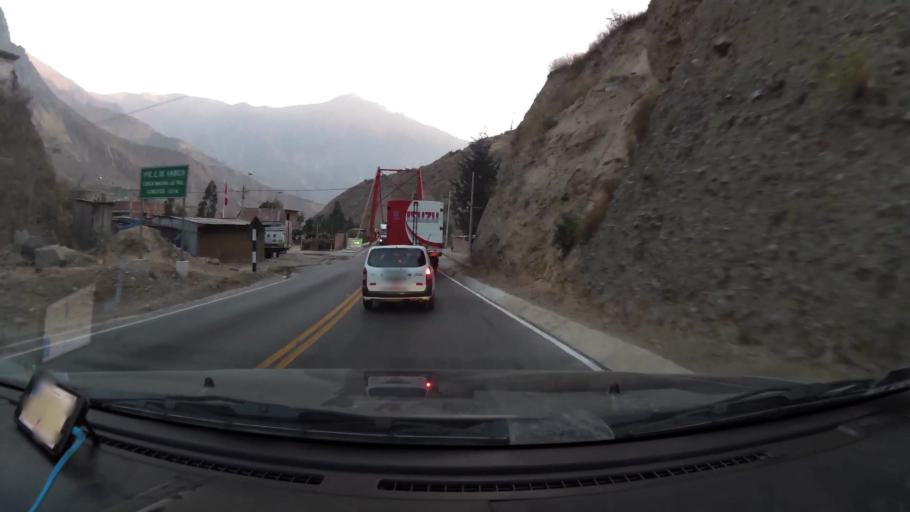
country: PE
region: Lima
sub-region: Provincia de Huarochiri
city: Surco
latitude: -11.8639
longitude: -76.4239
